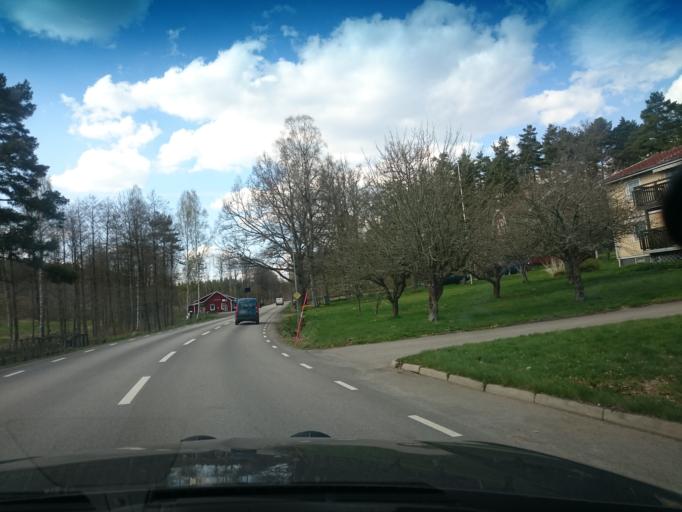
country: SE
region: Kronoberg
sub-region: Uppvidinge Kommun
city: Aseda
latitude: 57.3437
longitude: 15.2726
